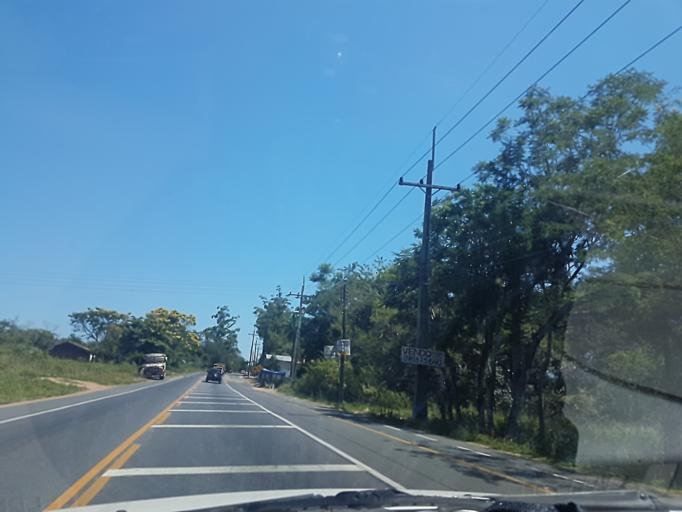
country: PY
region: Central
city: Aregua
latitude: -25.2292
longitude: -57.4179
